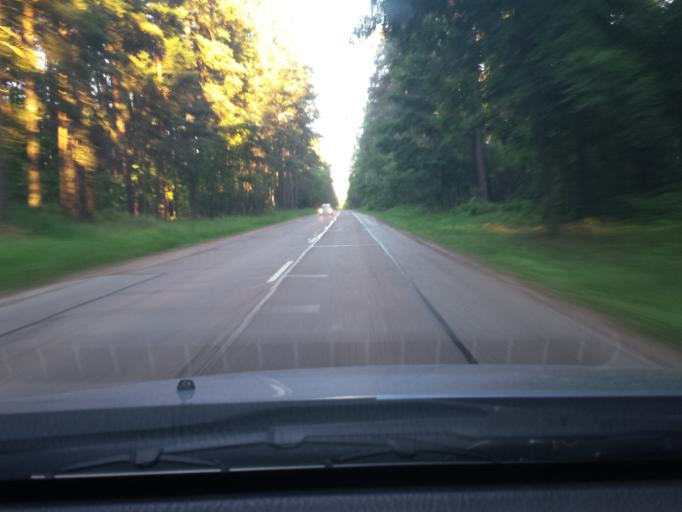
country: LV
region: Riga
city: Jaunciems
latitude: 57.0225
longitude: 24.1999
